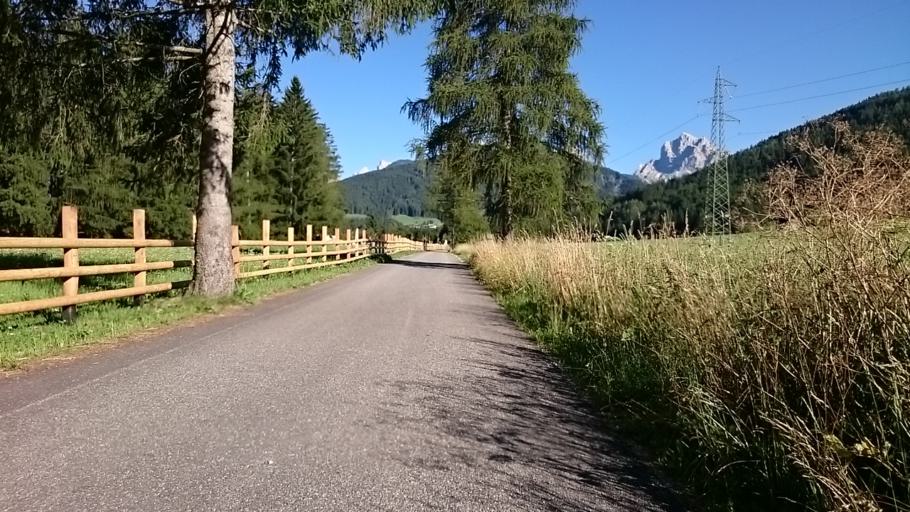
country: IT
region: Trentino-Alto Adige
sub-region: Bolzano
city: Monguelfo
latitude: 46.7441
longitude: 12.1234
